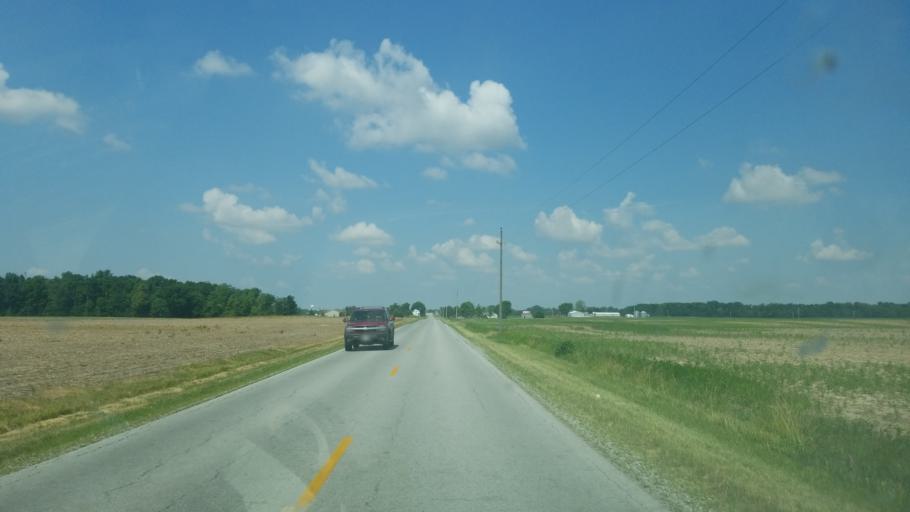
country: US
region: Ohio
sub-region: Auglaize County
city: Wapakoneta
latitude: 40.5702
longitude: -84.1531
